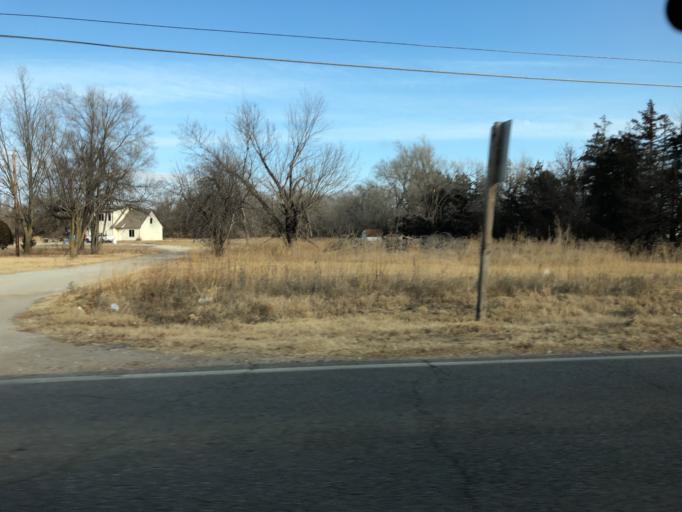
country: US
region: Kansas
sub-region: Reno County
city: South Hutchinson
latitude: 38.0573
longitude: -97.9792
